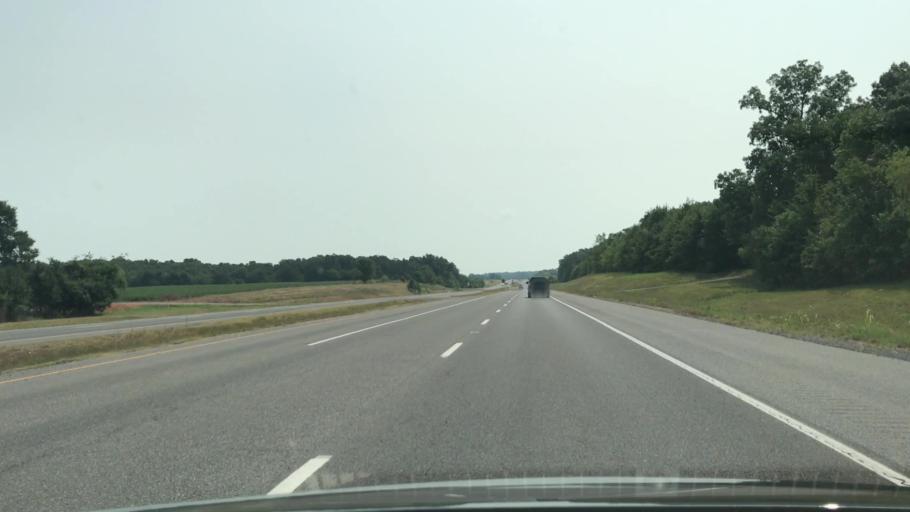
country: US
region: Kentucky
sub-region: Calloway County
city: Murray
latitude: 36.6507
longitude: -88.2687
